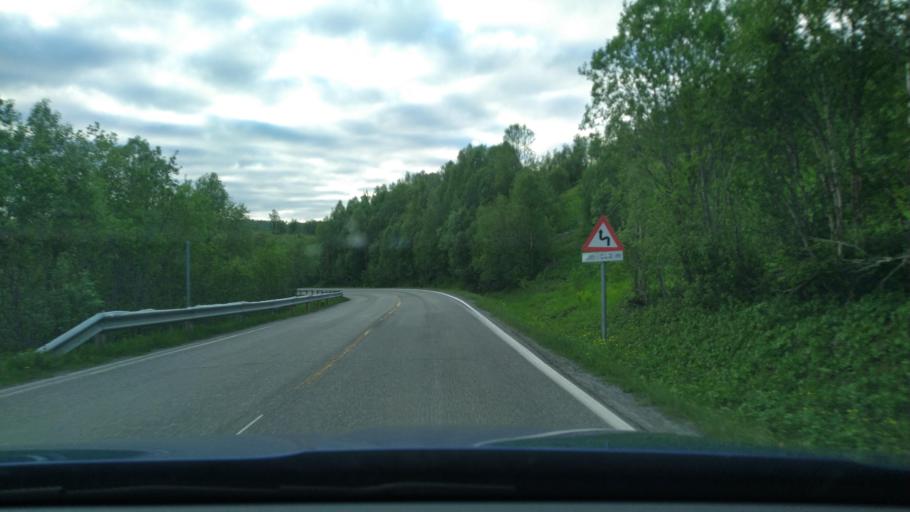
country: NO
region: Troms
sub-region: Sorreisa
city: Sorreisa
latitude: 69.0941
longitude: 18.3390
